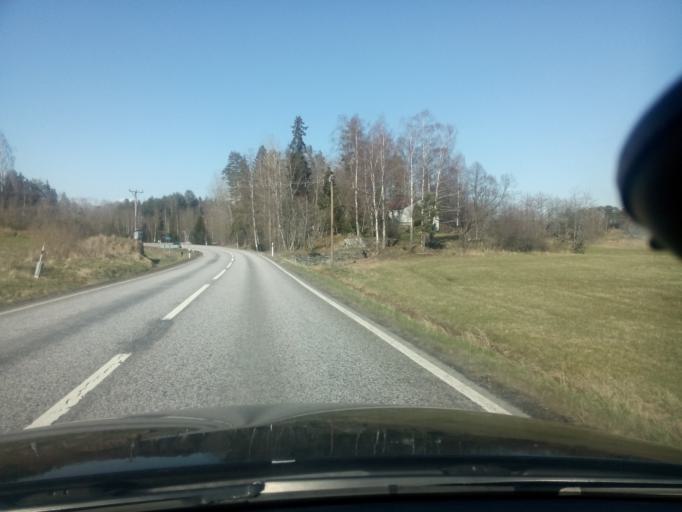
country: SE
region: Soedermanland
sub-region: Nykopings Kommun
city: Stigtomta
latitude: 58.9529
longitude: 16.8560
